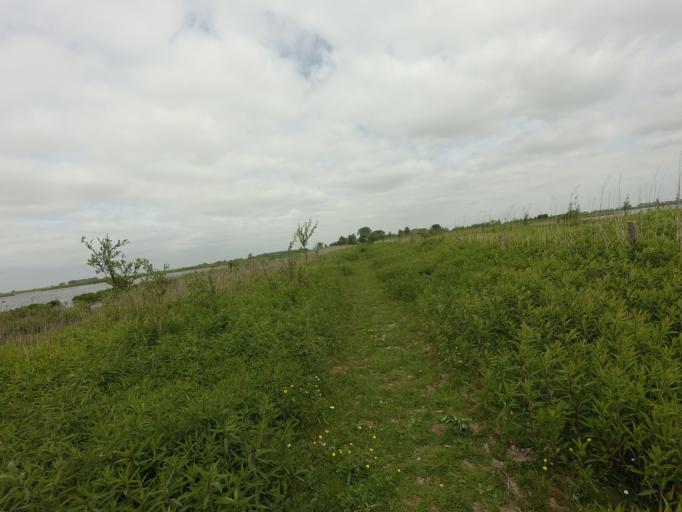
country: NL
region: South Holland
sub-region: Gemeente Spijkenisse
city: Spijkenisse
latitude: 51.7385
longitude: 4.3170
